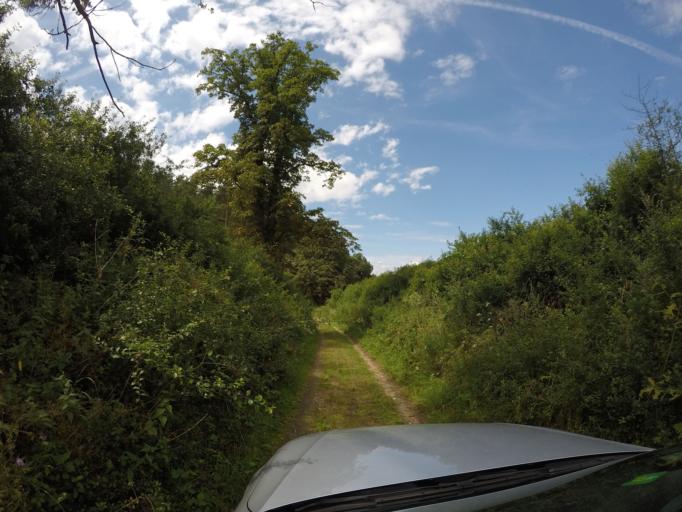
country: DE
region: Mecklenburg-Vorpommern
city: Mollenhagen
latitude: 53.4824
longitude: 12.9407
